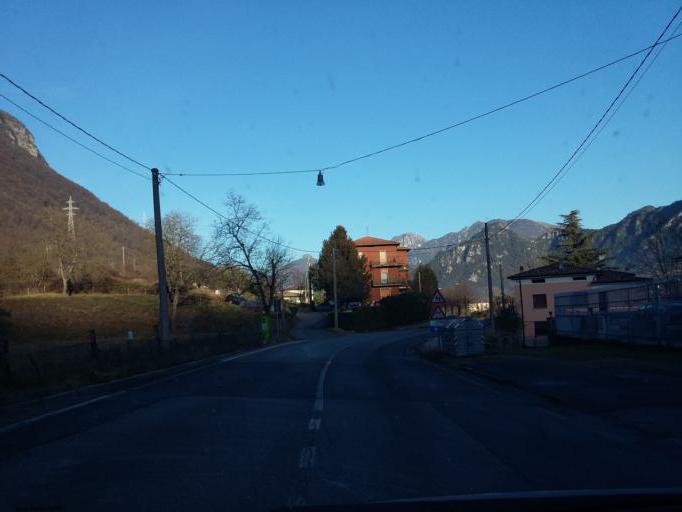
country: IT
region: Lombardy
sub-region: Provincia di Brescia
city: Idro
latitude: 45.7354
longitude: 10.4595
